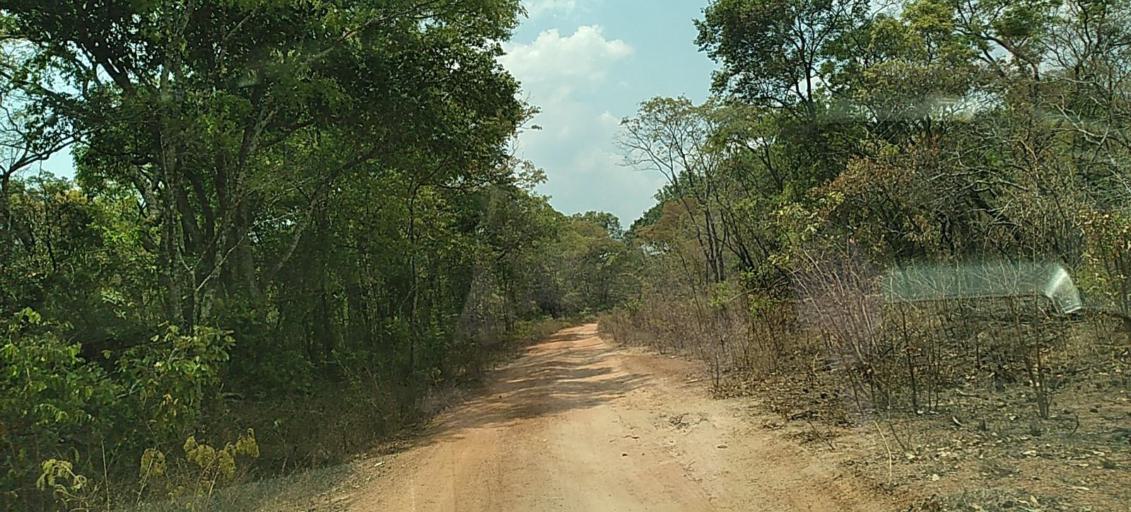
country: ZM
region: Copperbelt
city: Chingola
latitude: -12.8119
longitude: 27.6392
